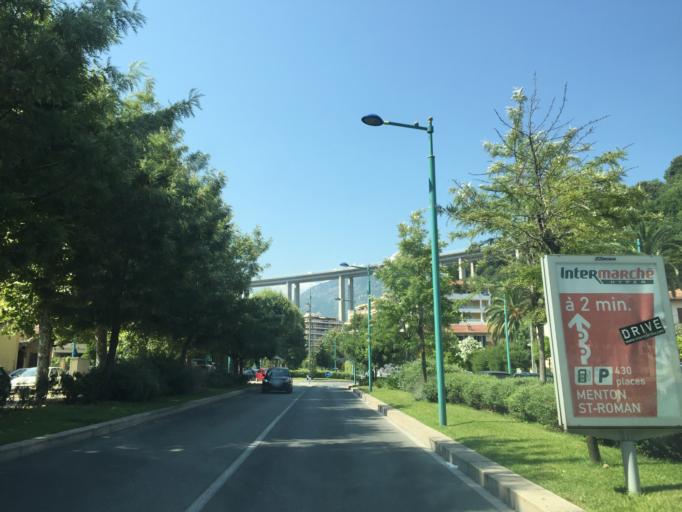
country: FR
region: Provence-Alpes-Cote d'Azur
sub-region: Departement des Alpes-Maritimes
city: Menton
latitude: 43.7927
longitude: 7.4918
